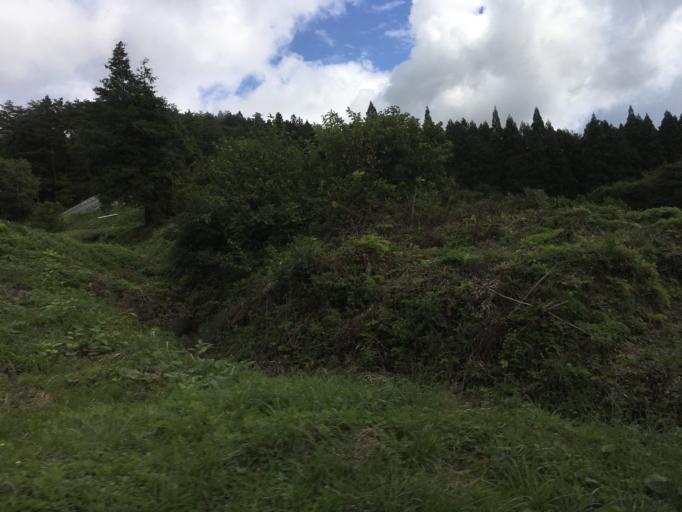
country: JP
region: Iwate
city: Ichinoseki
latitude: 38.8206
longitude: 141.3705
